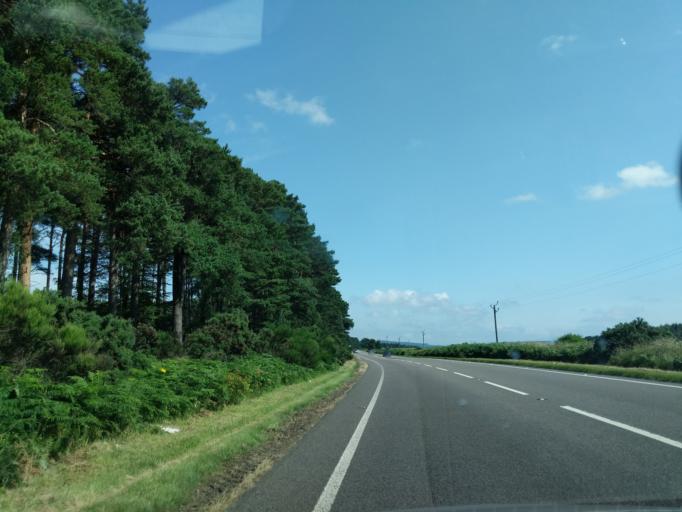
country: GB
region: Scotland
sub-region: Moray
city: Lhanbryd
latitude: 57.6326
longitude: -3.1839
